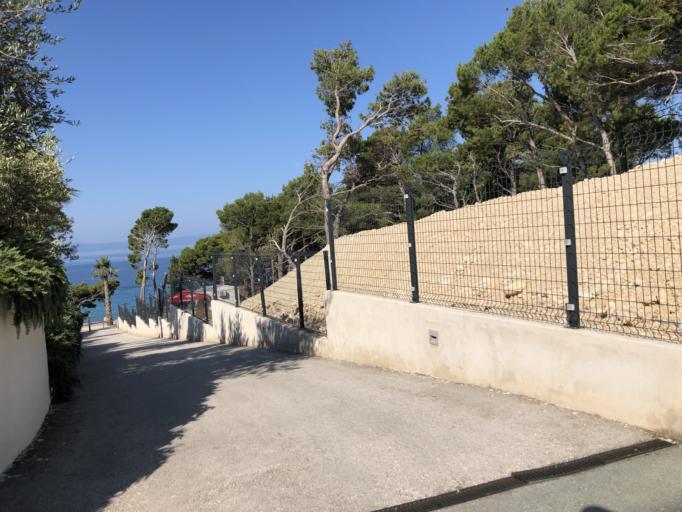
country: HR
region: Splitsko-Dalmatinska
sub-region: Grad Makarska
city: Makarska
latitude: 43.3072
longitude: 17.0016
